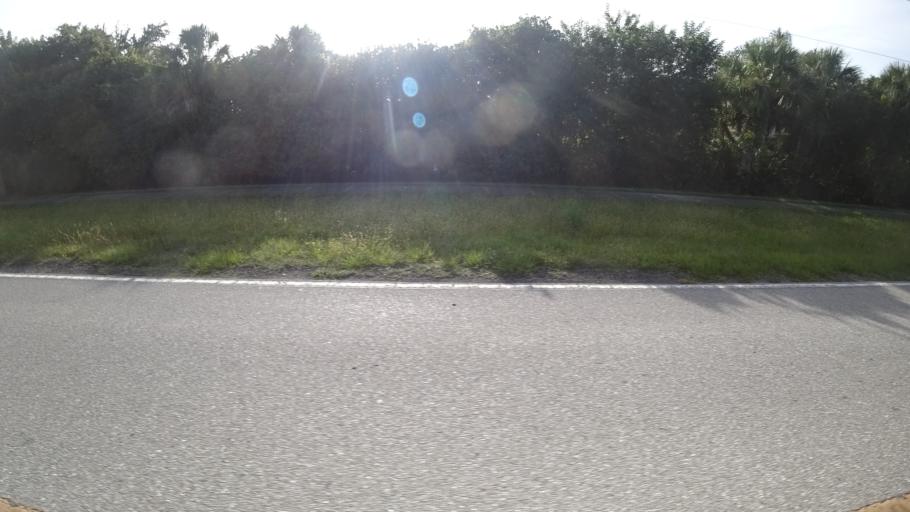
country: US
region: Florida
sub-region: Sarasota County
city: Desoto Lakes
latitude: 27.4318
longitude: -82.4712
